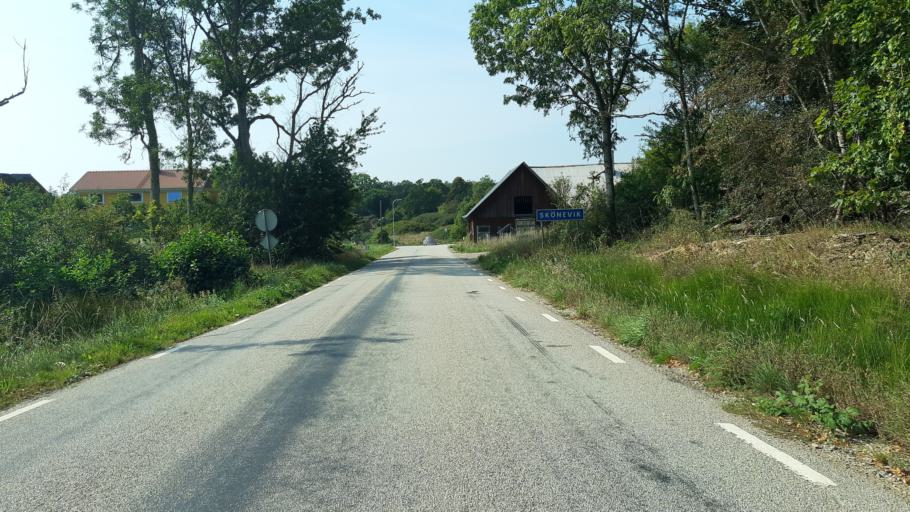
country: SE
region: Blekinge
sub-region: Ronneby Kommun
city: Brakne-Hoby
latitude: 56.1681
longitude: 15.1821
